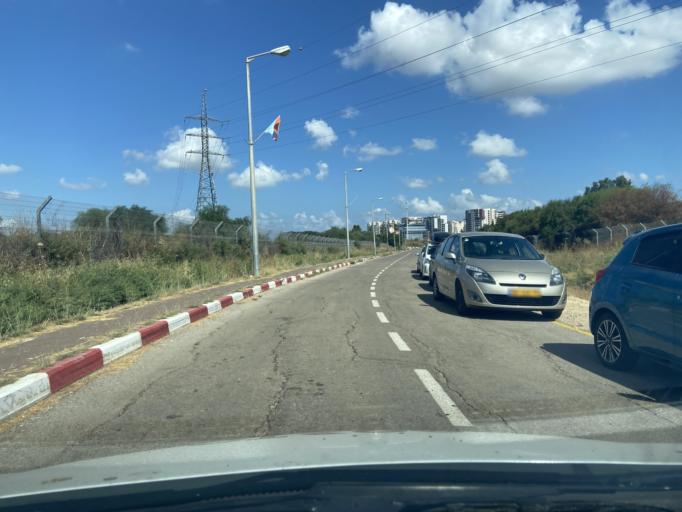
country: IL
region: Central District
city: Yehud
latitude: 32.0239
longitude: 34.8961
